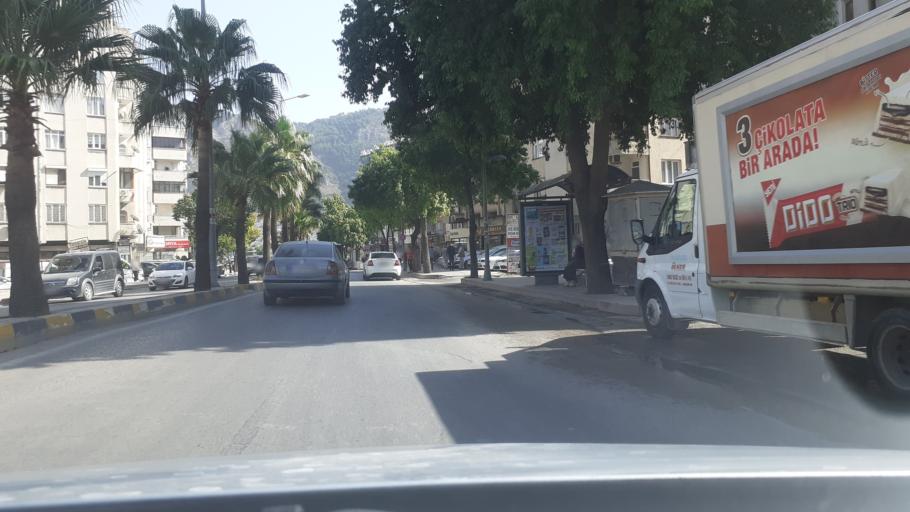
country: TR
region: Hatay
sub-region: Antakya Ilcesi
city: Antakya
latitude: 36.2107
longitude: 36.1600
